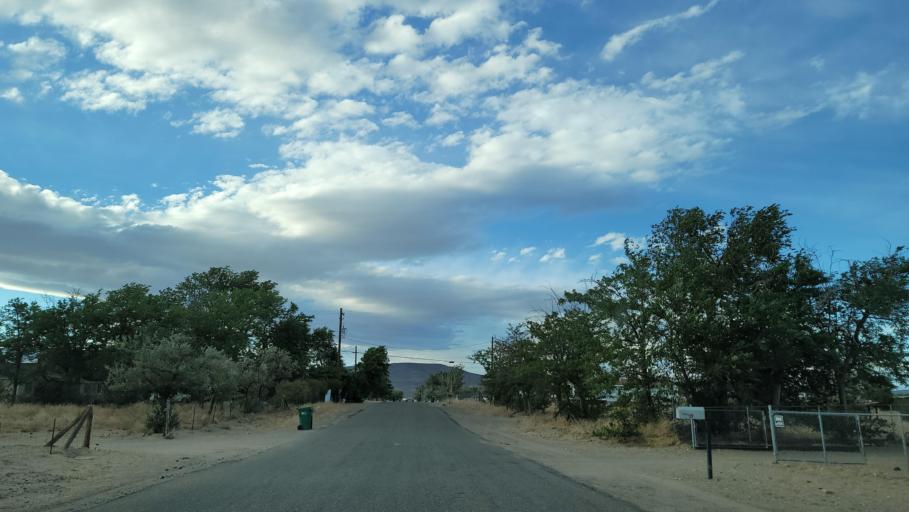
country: US
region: Nevada
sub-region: Lyon County
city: Silver Springs
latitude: 39.3909
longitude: -119.2372
